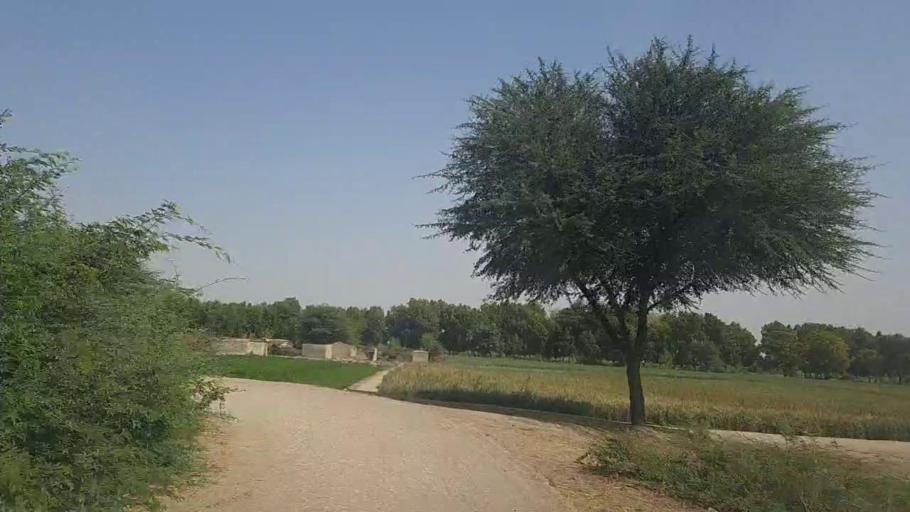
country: PK
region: Sindh
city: Naukot
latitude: 24.8405
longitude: 69.4172
